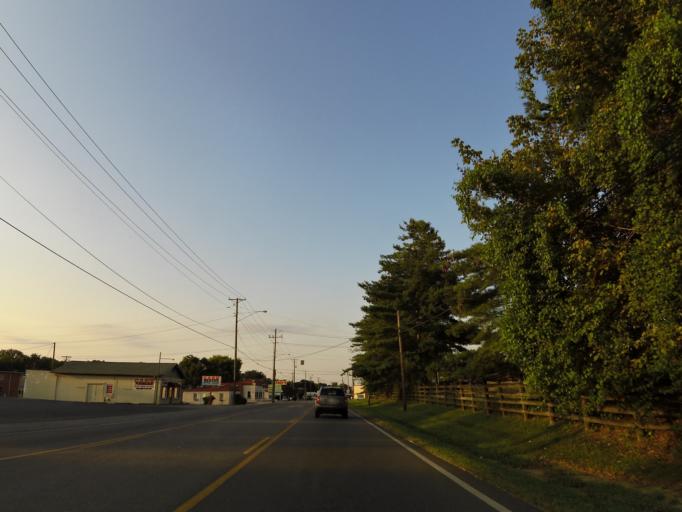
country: US
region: Tennessee
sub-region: Monroe County
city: Sweetwater
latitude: 35.5926
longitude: -84.4683
